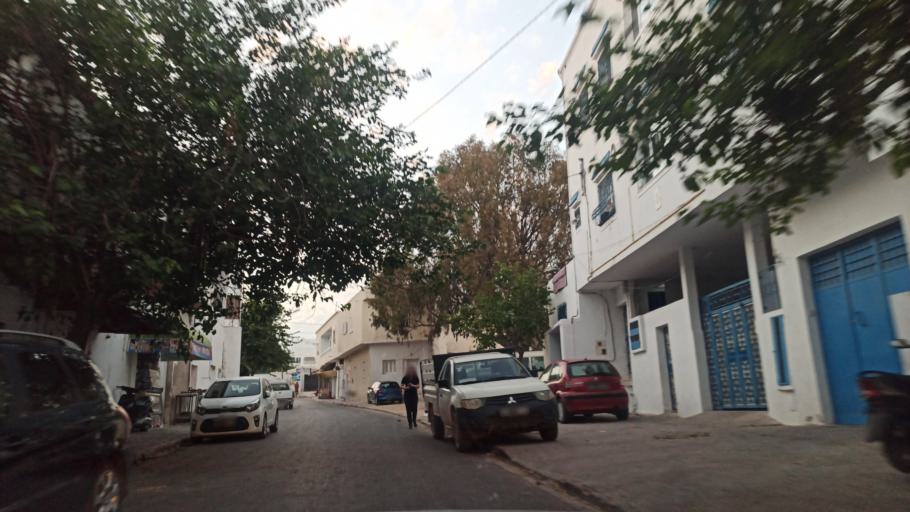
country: TN
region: Nabul
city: Al Hammamat
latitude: 36.4049
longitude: 10.6206
